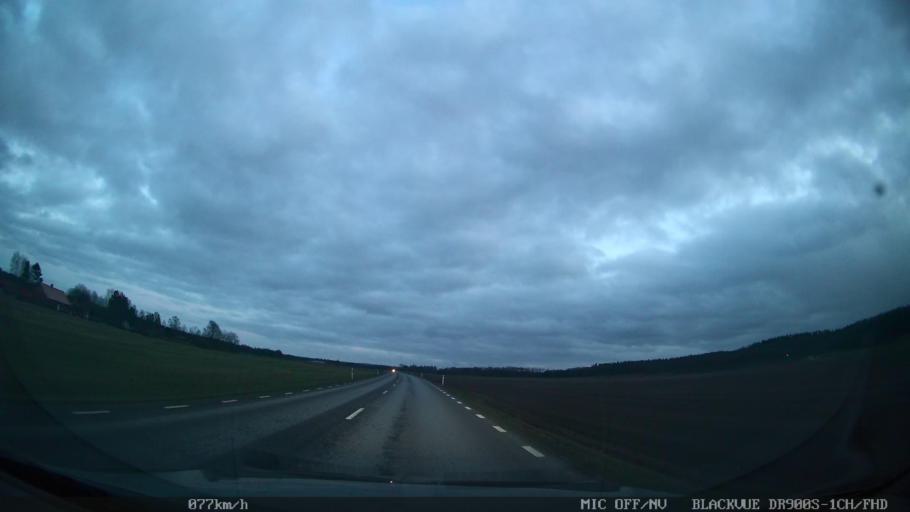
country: SE
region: Skane
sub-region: Hassleholms Kommun
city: Bjarnum
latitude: 56.1933
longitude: 13.6692
